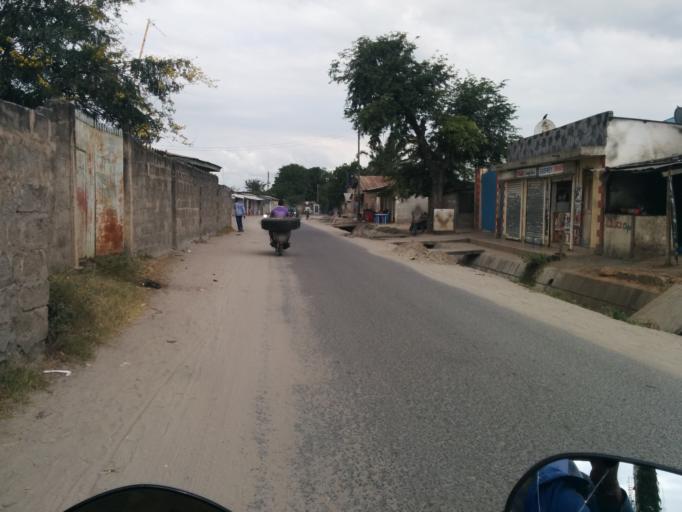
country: TZ
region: Dar es Salaam
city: Dar es Salaam
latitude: -6.8664
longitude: 39.2499
